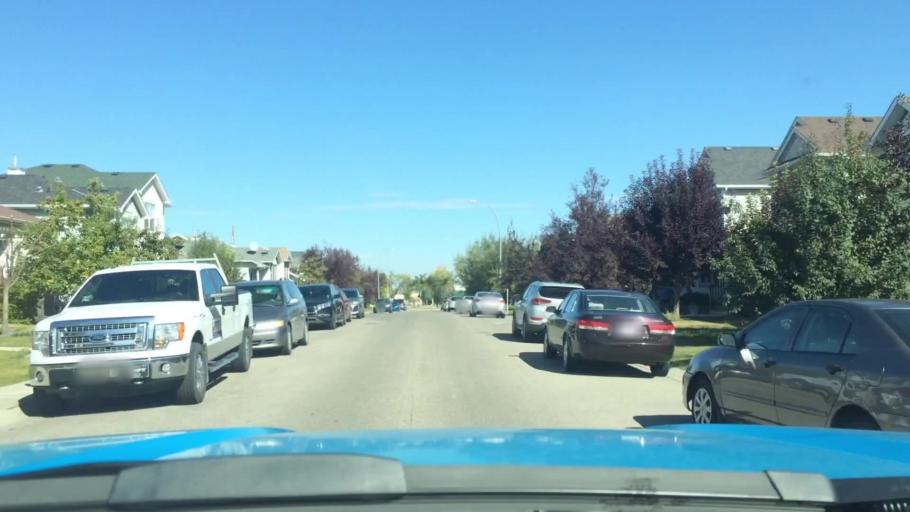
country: CA
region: Alberta
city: Calgary
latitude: 50.9051
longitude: -114.1091
